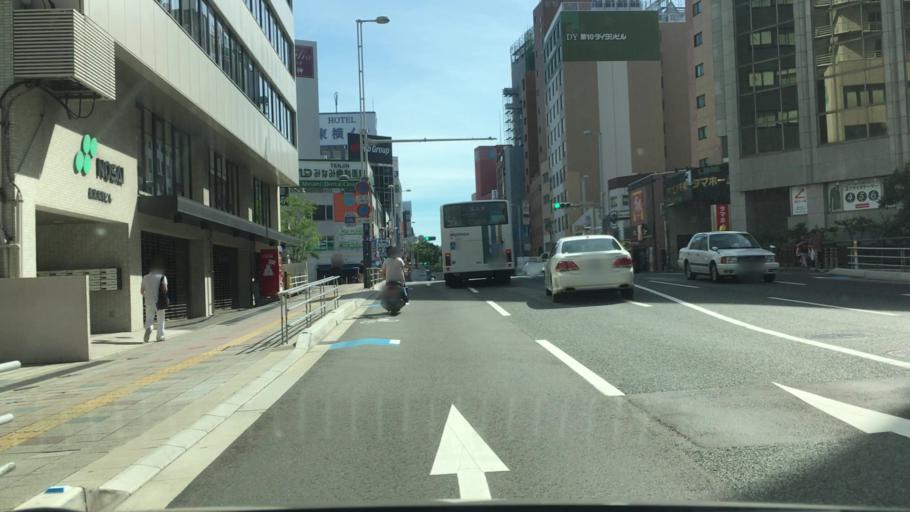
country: JP
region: Fukuoka
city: Fukuoka-shi
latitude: 33.5889
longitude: 130.4031
